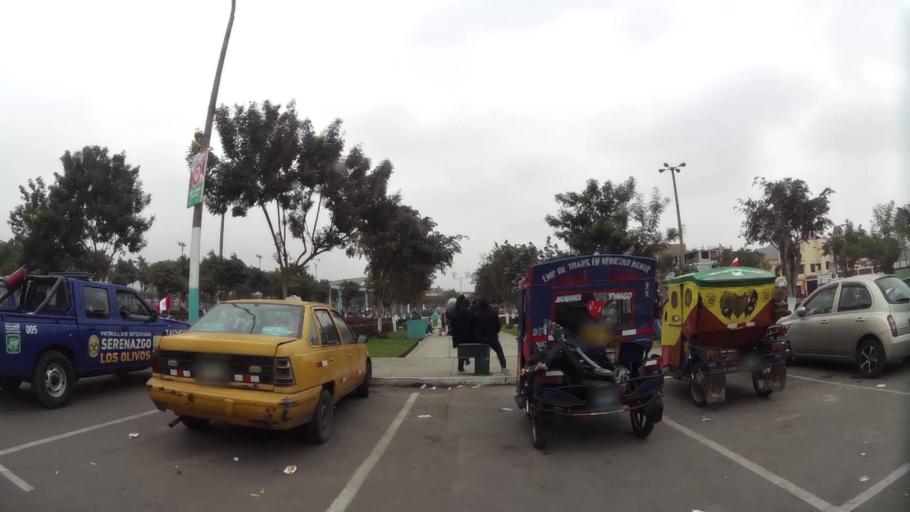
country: PE
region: Lima
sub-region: Lima
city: Independencia
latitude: -11.9341
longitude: -77.0773
